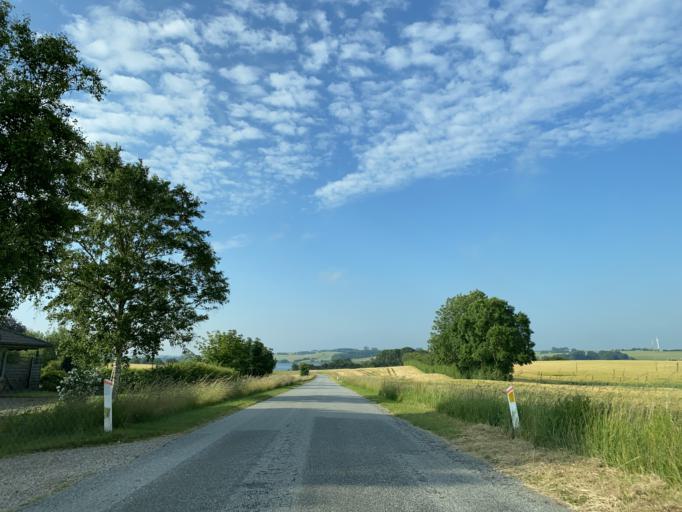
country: DK
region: South Denmark
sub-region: Haderslev Kommune
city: Haderslev
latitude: 55.1780
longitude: 9.4815
